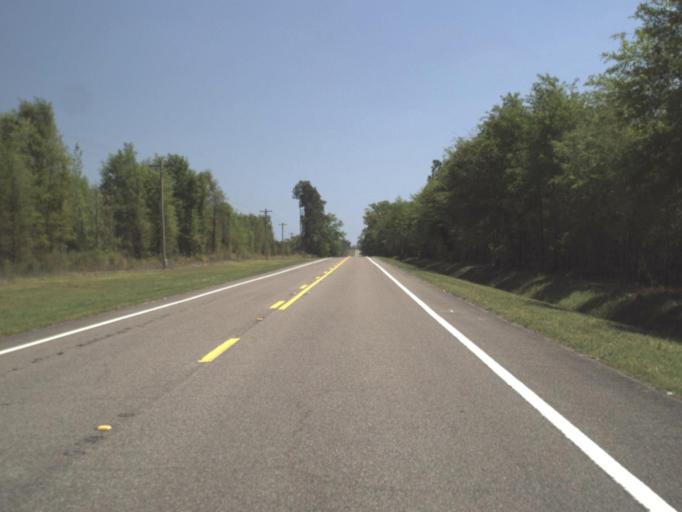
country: US
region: Alabama
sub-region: Escambia County
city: East Brewton
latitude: 30.9277
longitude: -87.0543
